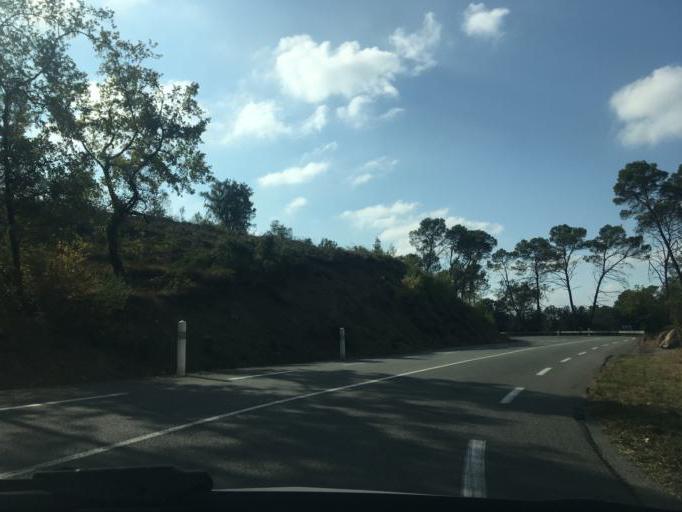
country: FR
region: Provence-Alpes-Cote d'Azur
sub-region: Departement du Var
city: Flayosc
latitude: 43.4959
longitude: 6.4004
